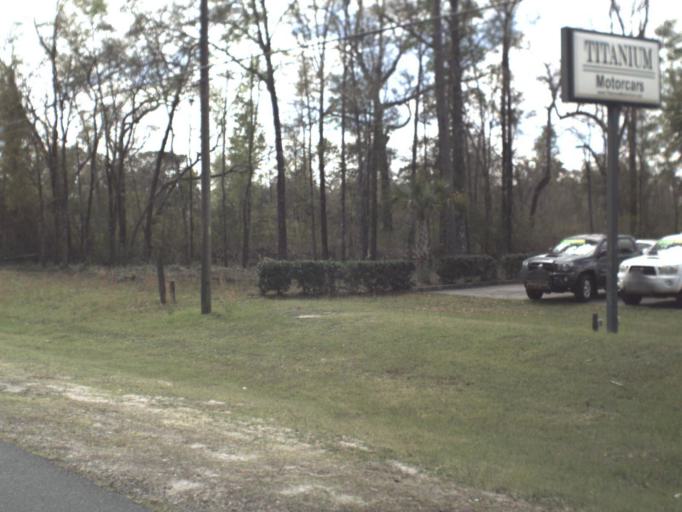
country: US
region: Florida
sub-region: Wakulla County
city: Crawfordville
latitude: 30.2430
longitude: -84.3624
